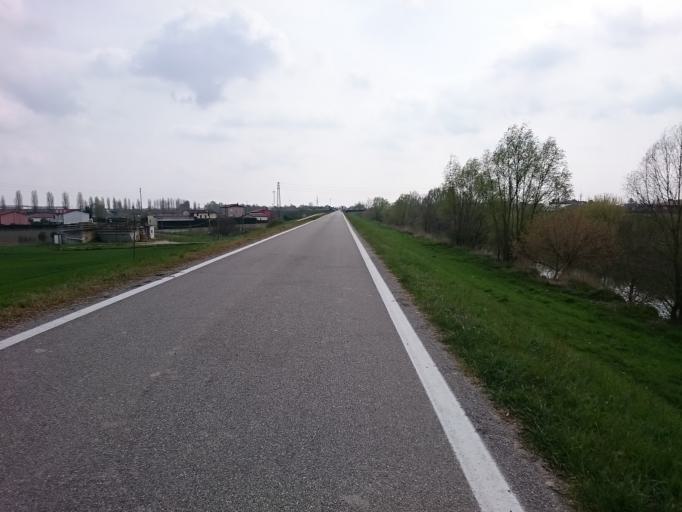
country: IT
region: Veneto
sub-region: Provincia di Padova
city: Bovolenta
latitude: 45.2750
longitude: 11.9359
